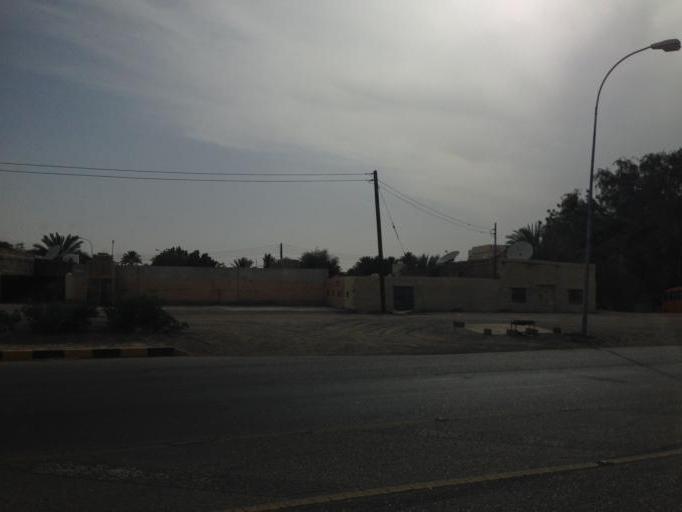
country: OM
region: Ash Sharqiyah
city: Badiyah
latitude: 22.5034
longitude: 58.7481
